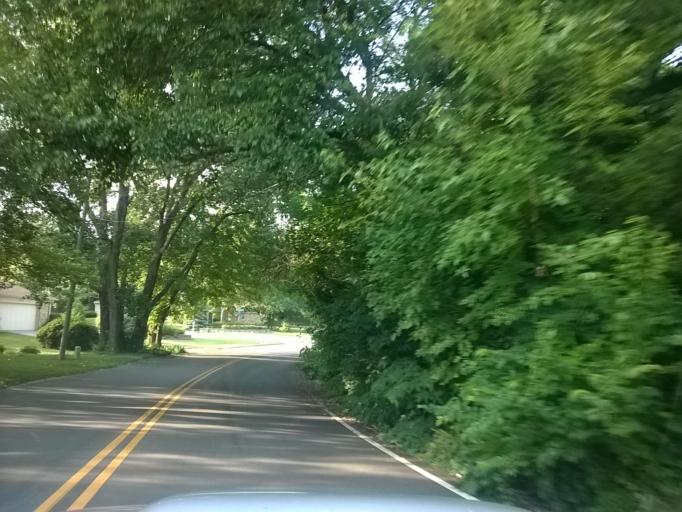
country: US
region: Indiana
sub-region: Hamilton County
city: Carmel
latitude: 39.9484
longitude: -86.0983
